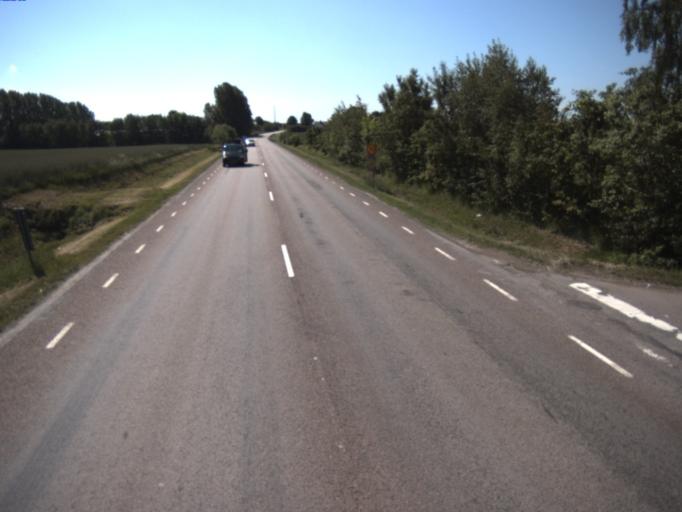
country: SE
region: Skane
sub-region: Helsingborg
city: Barslov
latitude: 56.0238
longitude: 12.7930
